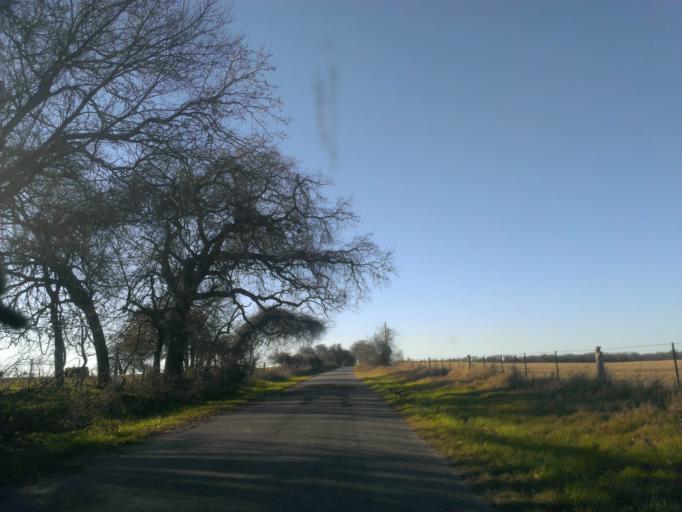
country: US
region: Texas
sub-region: Bastrop County
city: Elgin
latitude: 30.3484
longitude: -97.2947
